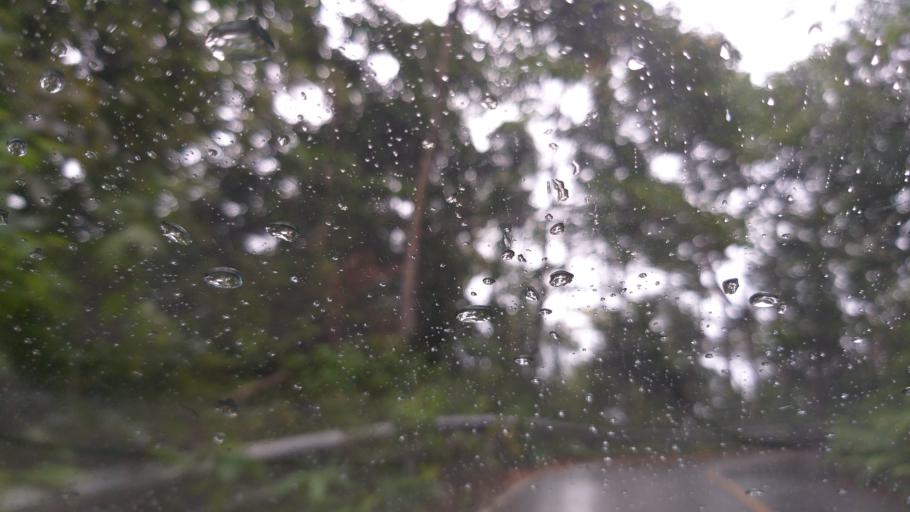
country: TH
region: Trat
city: Ko Chang Tai
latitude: 11.9788
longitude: 102.3222
